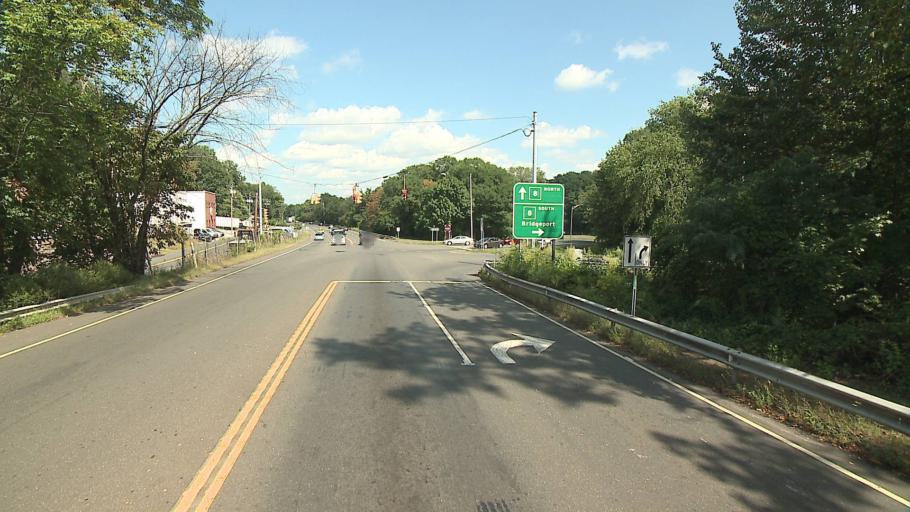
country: US
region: Connecticut
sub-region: Fairfield County
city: Shelton
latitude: 41.3019
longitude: -73.1027
